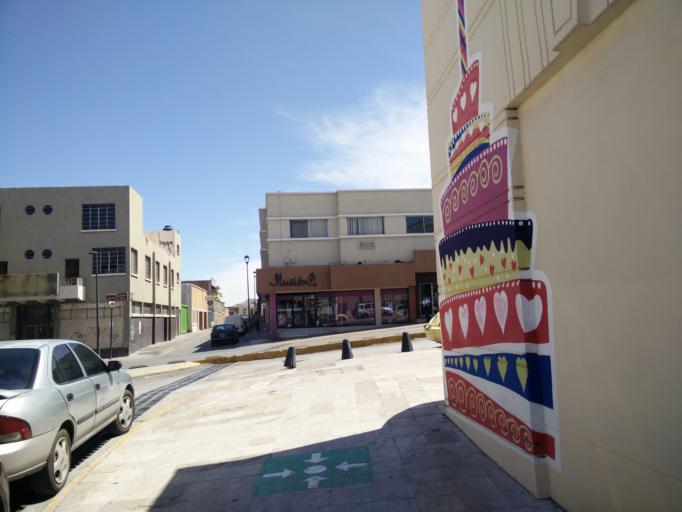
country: MX
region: Chihuahua
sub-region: Chihuahua
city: Chihuahua
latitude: 28.6345
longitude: -106.0741
